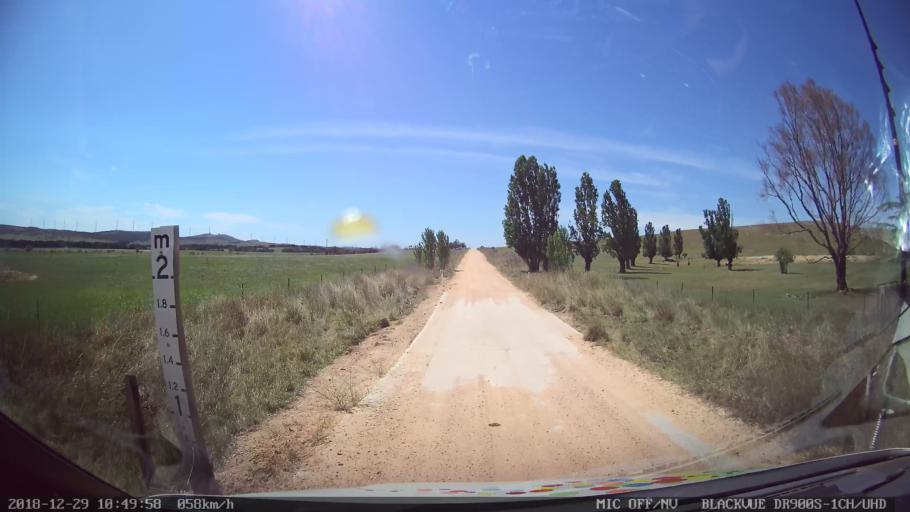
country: AU
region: New South Wales
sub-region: Palerang
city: Bungendore
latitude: -35.0789
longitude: 149.5194
